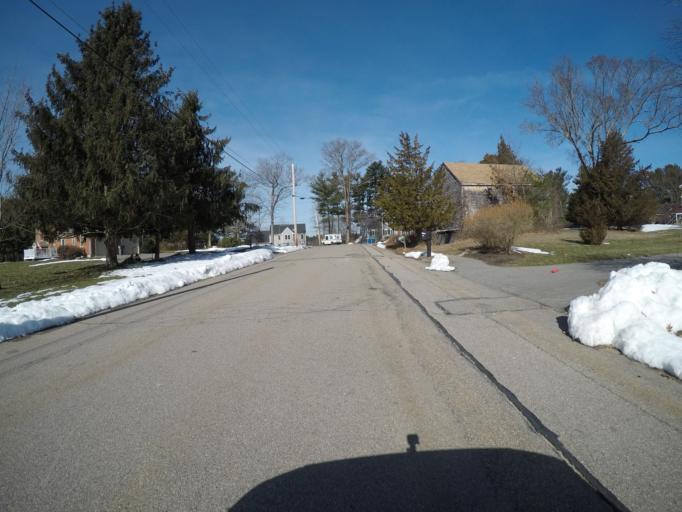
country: US
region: Massachusetts
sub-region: Bristol County
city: Easton
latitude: 41.9962
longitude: -71.1228
